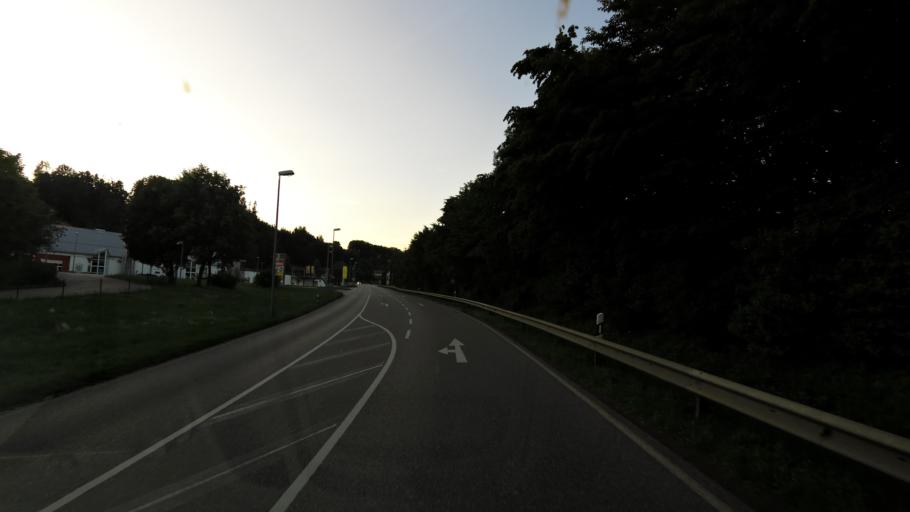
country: DE
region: Bavaria
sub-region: Upper Bavaria
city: Trostberg an der Alz
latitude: 48.0196
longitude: 12.5362
